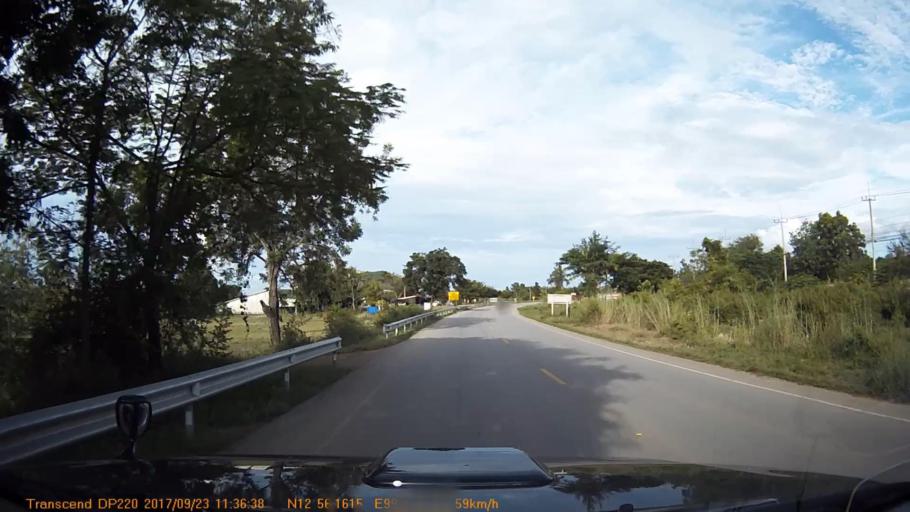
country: TH
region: Phetchaburi
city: Kaeng Krachan
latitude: 12.9360
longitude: 99.7522
